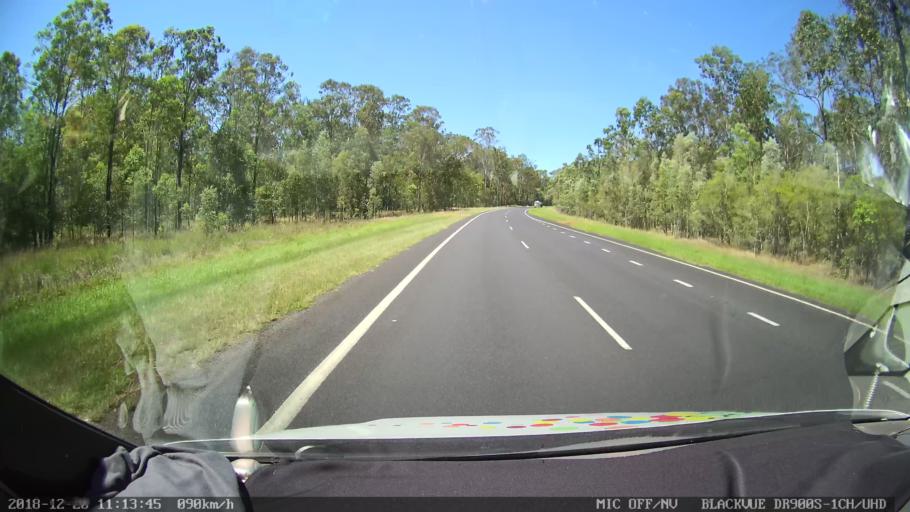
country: AU
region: New South Wales
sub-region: Richmond Valley
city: Casino
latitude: -28.9919
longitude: 153.0116
